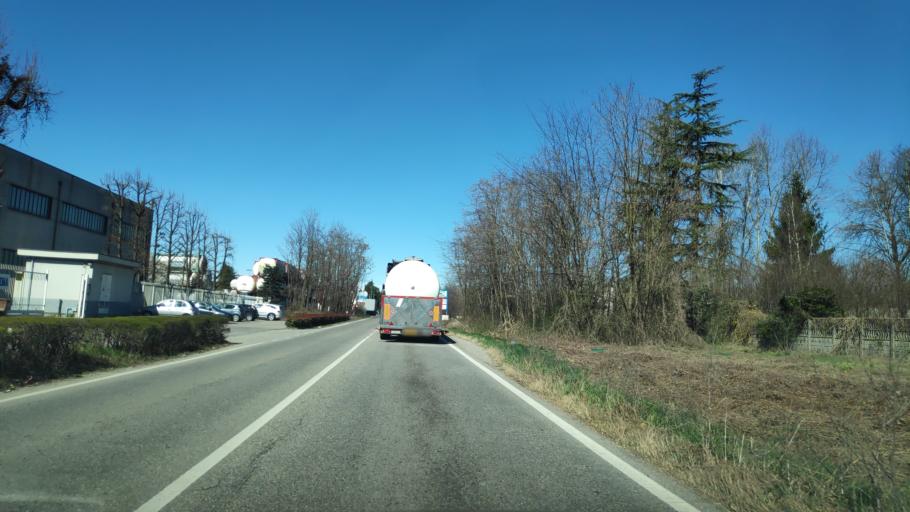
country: IT
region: Lombardy
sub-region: Provincia di Varese
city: Fagnano Olona-Bergoro
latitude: 45.6565
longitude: 8.8458
